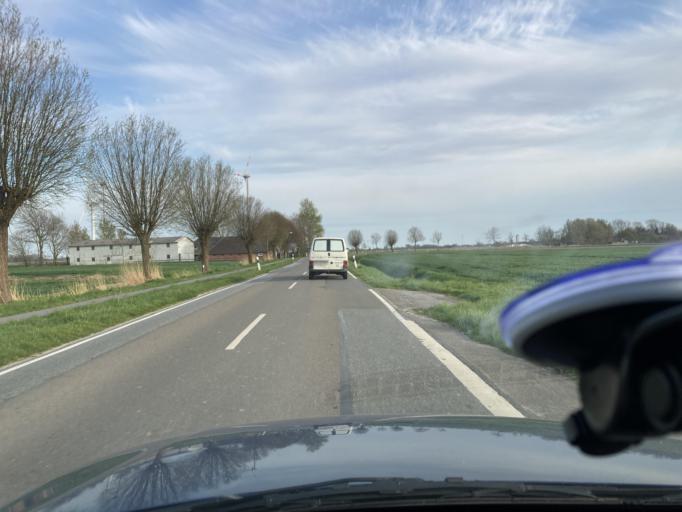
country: DE
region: Schleswig-Holstein
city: Schulp
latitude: 54.2318
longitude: 8.9314
